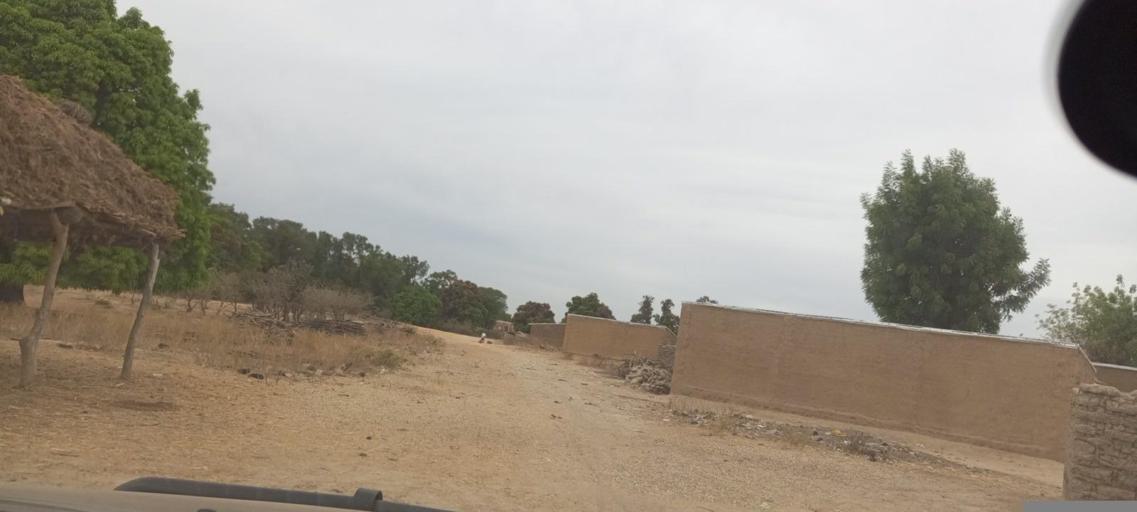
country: ML
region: Koulikoro
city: Kati
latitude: 12.7425
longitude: -8.3300
